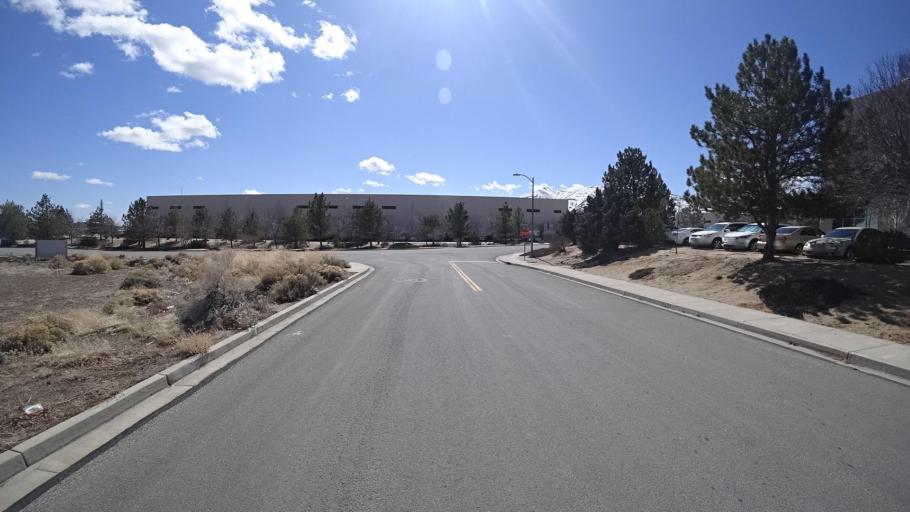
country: US
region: Nevada
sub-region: Washoe County
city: Lemmon Valley
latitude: 39.6550
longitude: -119.8998
